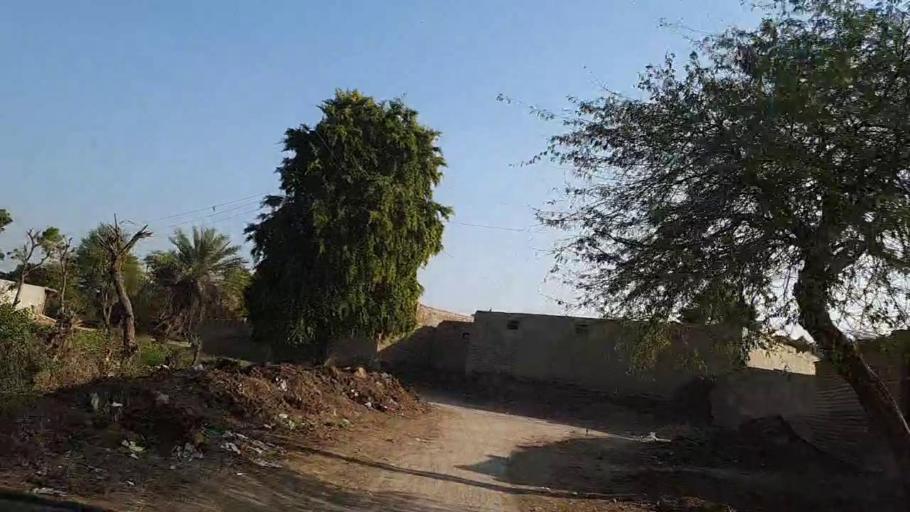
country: PK
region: Sindh
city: Sakrand
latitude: 26.1283
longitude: 68.2195
